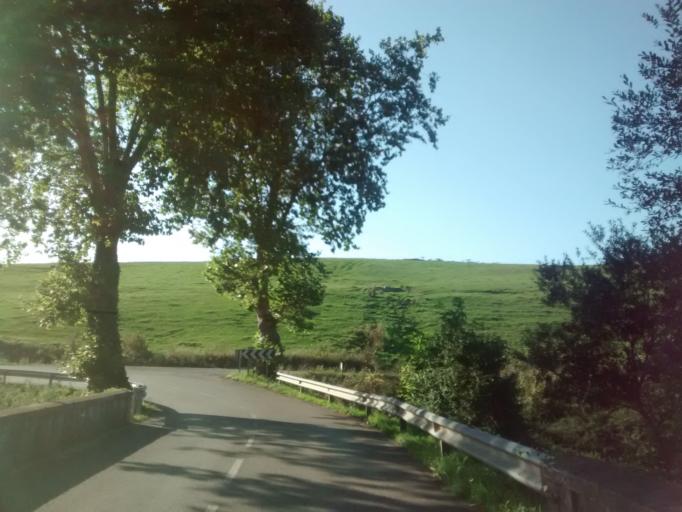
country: ES
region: Cantabria
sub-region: Provincia de Cantabria
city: Lierganes
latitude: 43.4161
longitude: -3.7427
